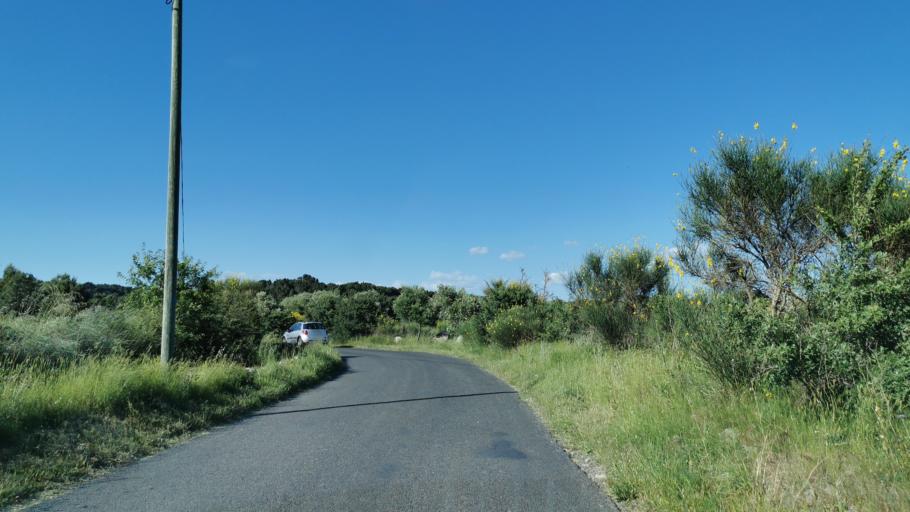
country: FR
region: Languedoc-Roussillon
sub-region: Departement de l'Aude
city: Gruissan
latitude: 43.1221
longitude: 3.0952
